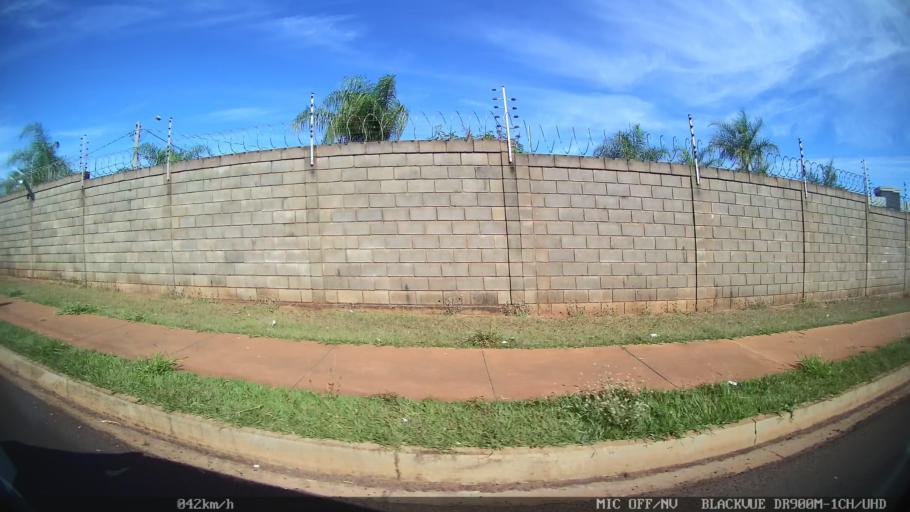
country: BR
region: Sao Paulo
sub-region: Sao Jose Do Rio Preto
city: Sao Jose do Rio Preto
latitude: -20.8063
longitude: -49.3312
